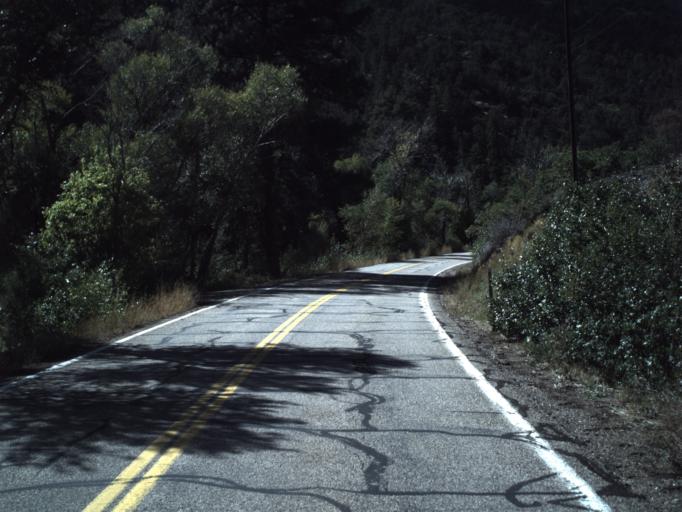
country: US
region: Utah
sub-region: Beaver County
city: Beaver
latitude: 38.2519
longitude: -112.5357
